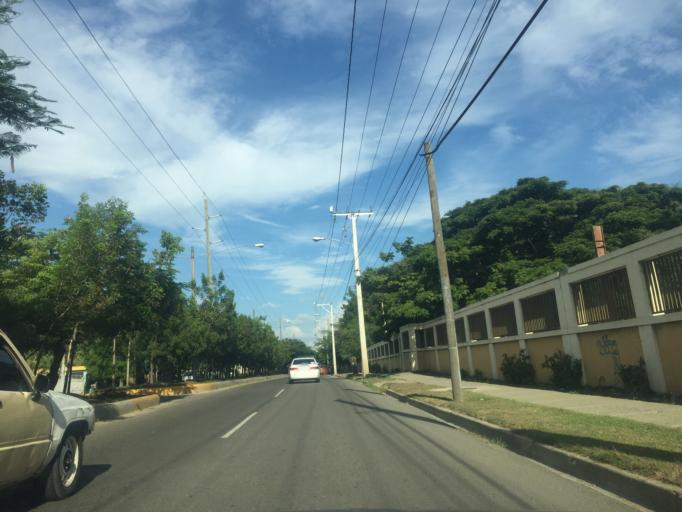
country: DO
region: Santiago
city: Santiago de los Caballeros
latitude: 19.4427
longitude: -70.7366
